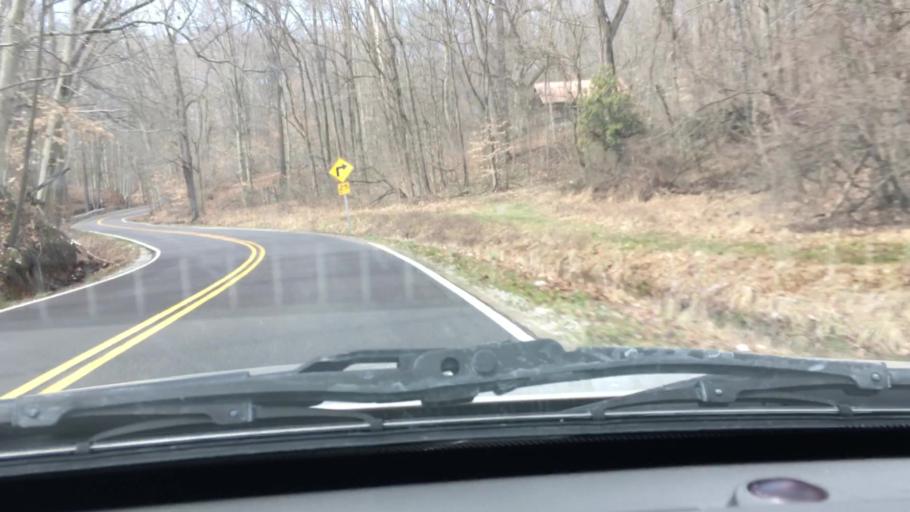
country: US
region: Indiana
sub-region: Morgan County
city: Martinsville
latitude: 39.4768
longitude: -86.4041
